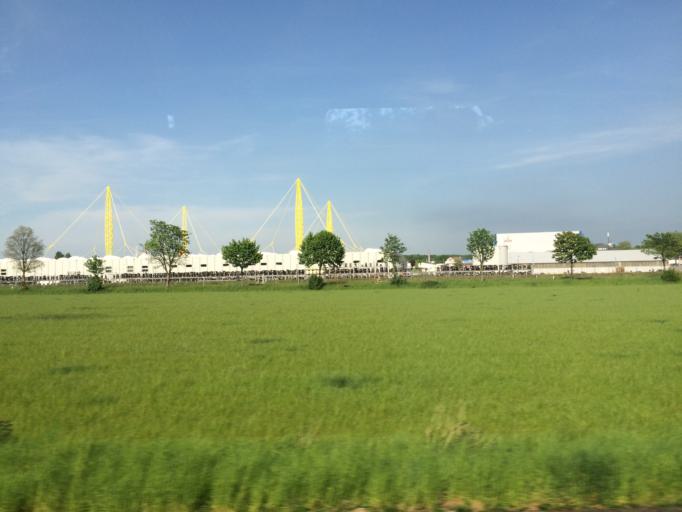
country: DE
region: North Rhine-Westphalia
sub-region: Regierungsbezirk Koln
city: Wahn-Heide
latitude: 50.8400
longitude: 7.0985
